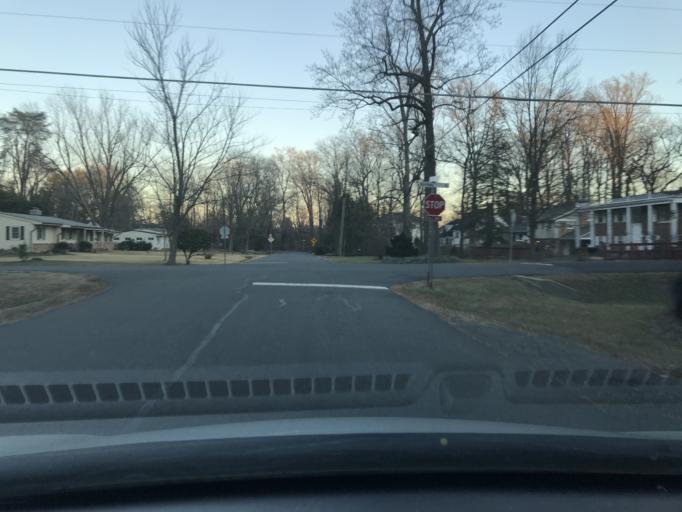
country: US
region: Virginia
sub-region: City of Fairfax
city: Fairfax
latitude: 38.8610
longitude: -77.3138
